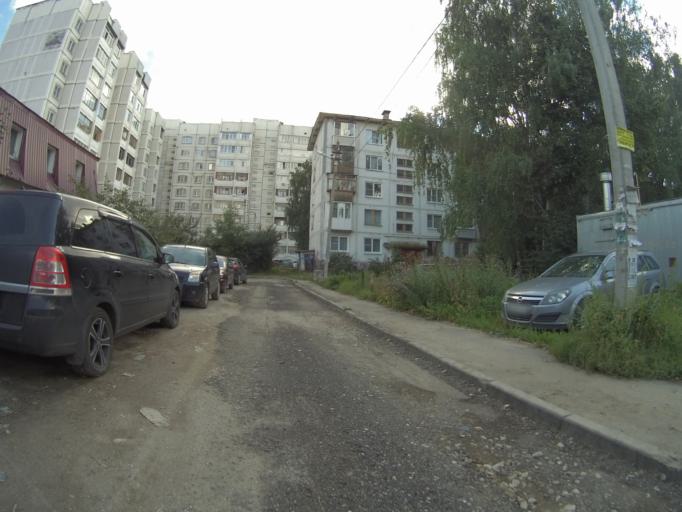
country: RU
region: Vladimir
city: Vladimir
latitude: 56.1364
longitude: 40.3648
